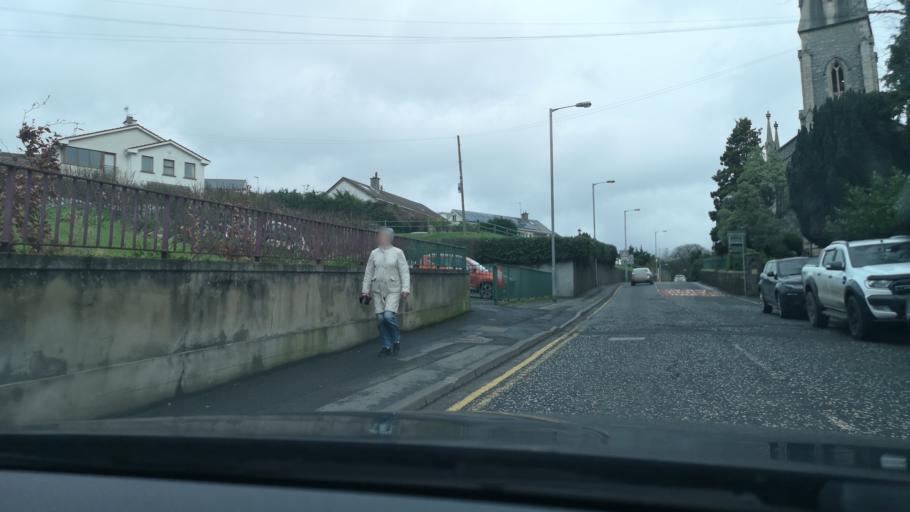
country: GB
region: Northern Ireland
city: Rostrevor
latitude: 54.1022
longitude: -6.1962
